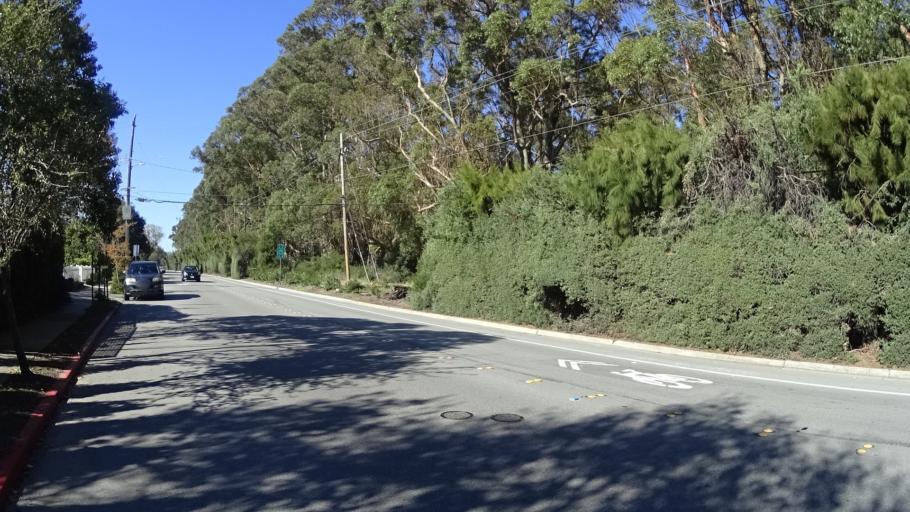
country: US
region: California
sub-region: San Mateo County
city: Burlingame
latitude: 37.5915
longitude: -122.3729
